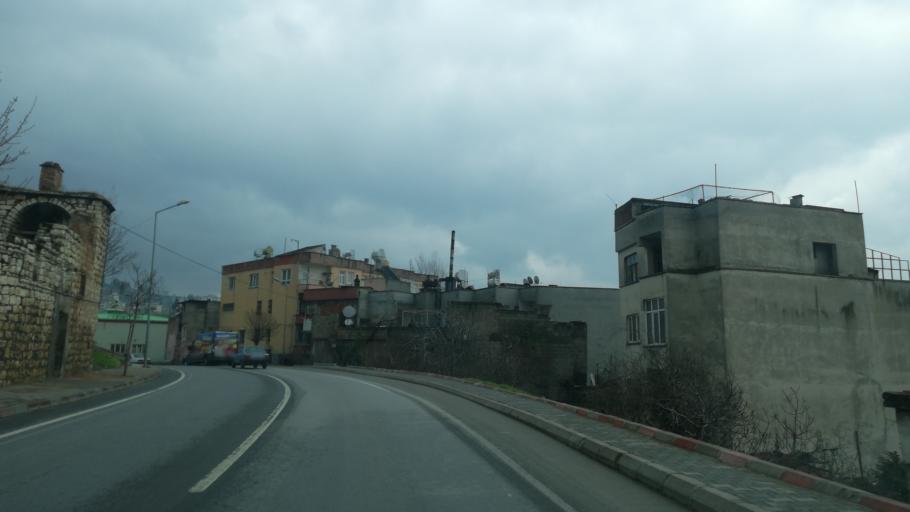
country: TR
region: Kahramanmaras
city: Kahramanmaras
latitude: 37.5927
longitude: 36.9319
